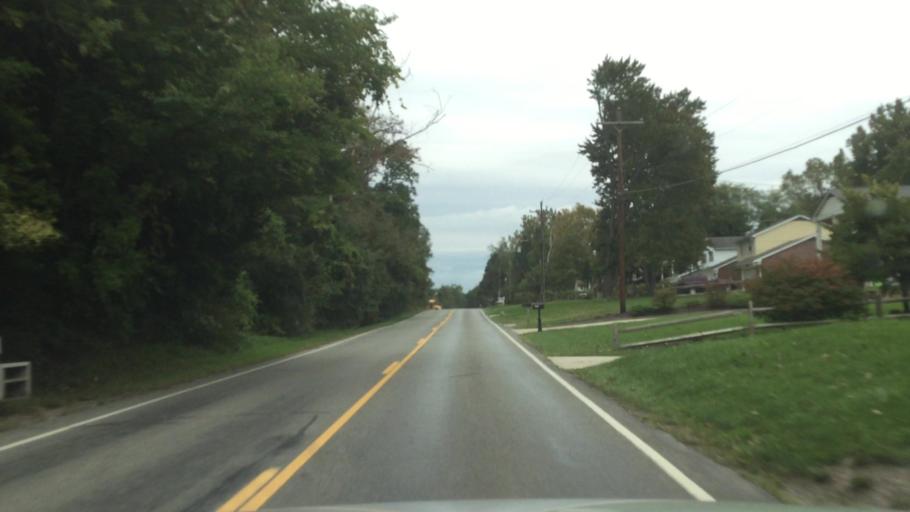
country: US
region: Michigan
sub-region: Livingston County
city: Whitmore Lake
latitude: 42.4790
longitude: -83.7672
